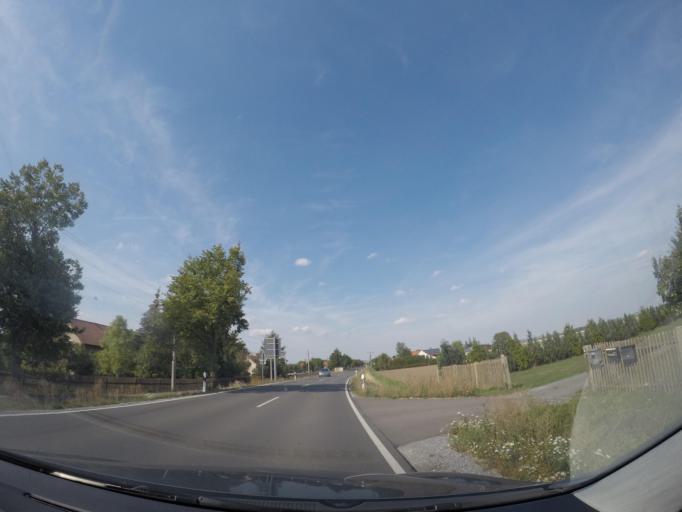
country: DE
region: Saxony-Anhalt
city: Langeln
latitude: 51.8798
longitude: 10.7705
